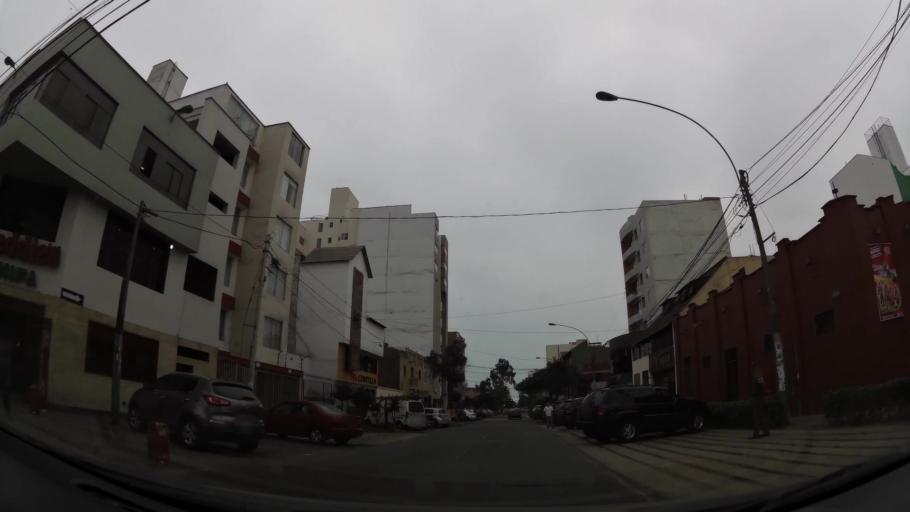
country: PE
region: Lima
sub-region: Lima
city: San Isidro
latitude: -12.0766
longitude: -77.0520
